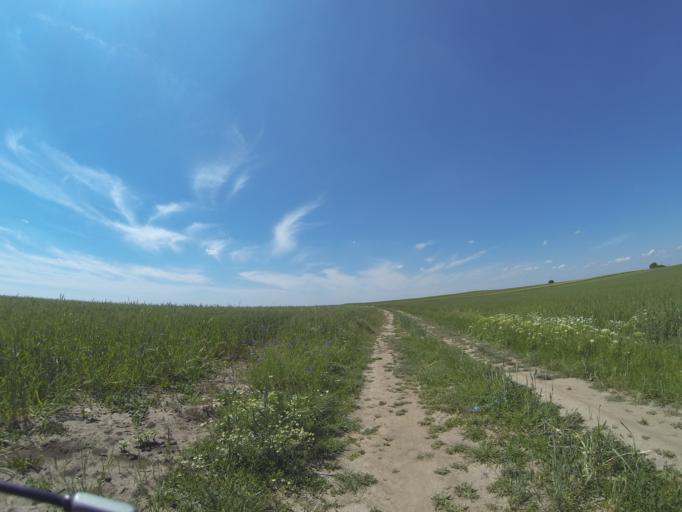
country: RO
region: Dolj
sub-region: Comuna Leu
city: Leu
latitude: 44.2154
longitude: 24.0217
